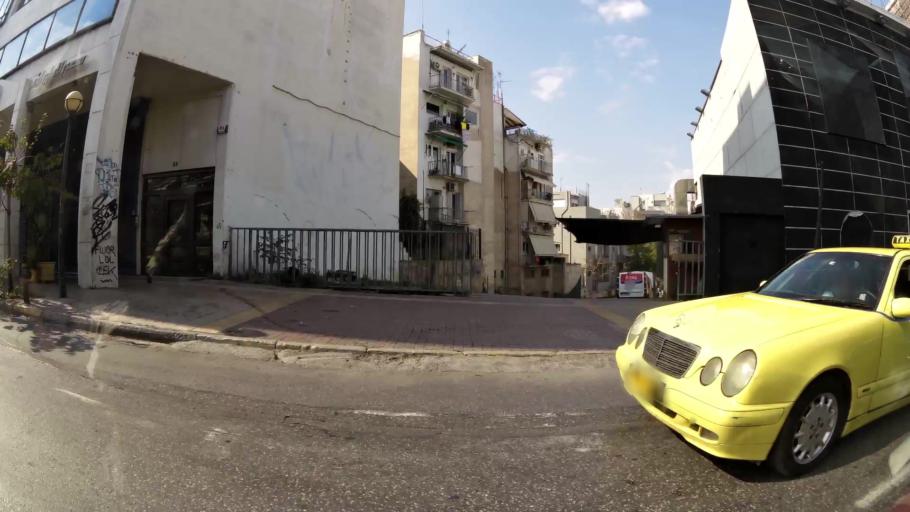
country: GR
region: Attica
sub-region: Nomarchia Athinas
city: Dhafni
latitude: 37.9657
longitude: 23.7329
